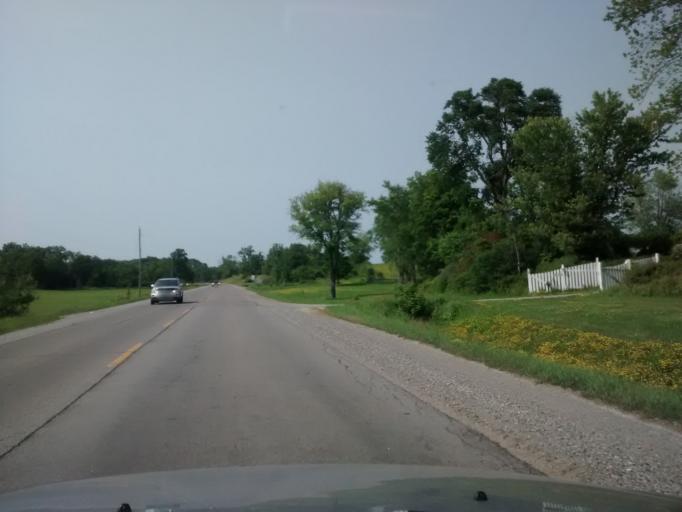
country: CA
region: Ontario
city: Ancaster
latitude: 42.9985
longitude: -79.8666
